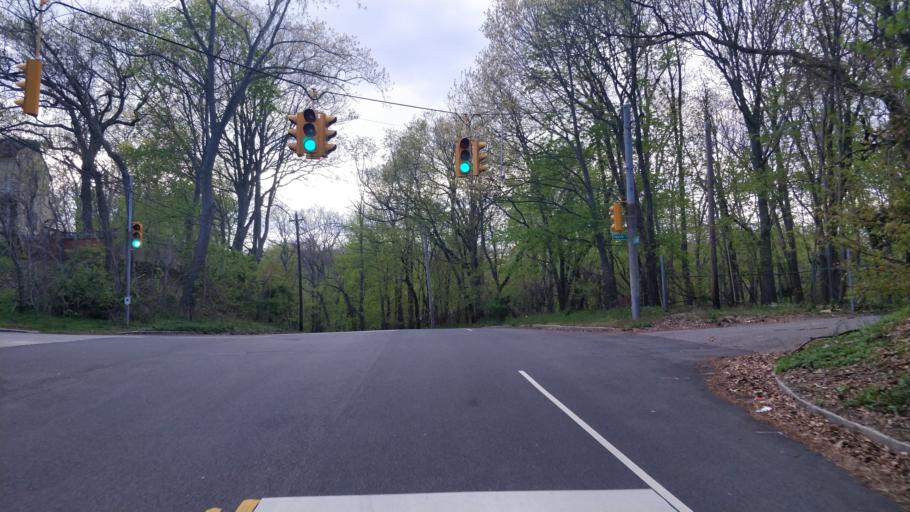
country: US
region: New York
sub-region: Suffolk County
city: Kings Park
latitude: 40.8943
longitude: -73.2310
